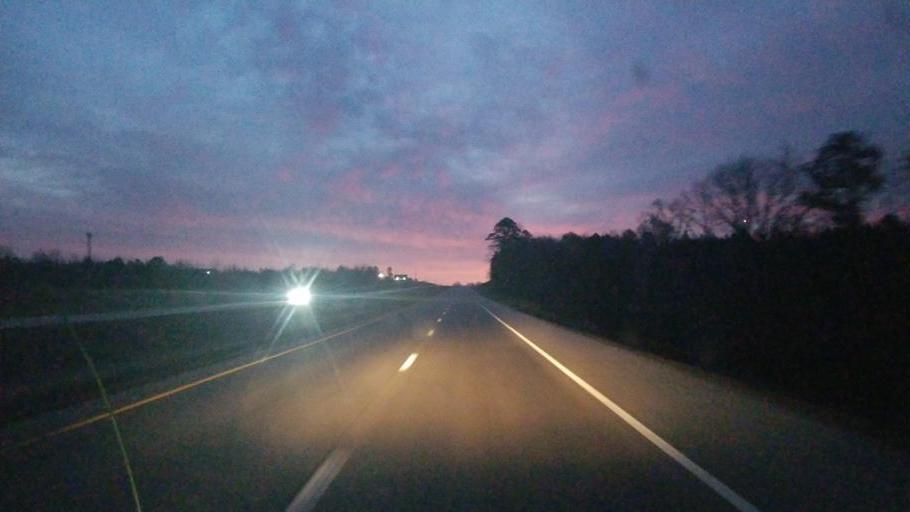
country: US
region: Missouri
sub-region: Shannon County
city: Winona
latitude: 36.9991
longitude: -91.4755
